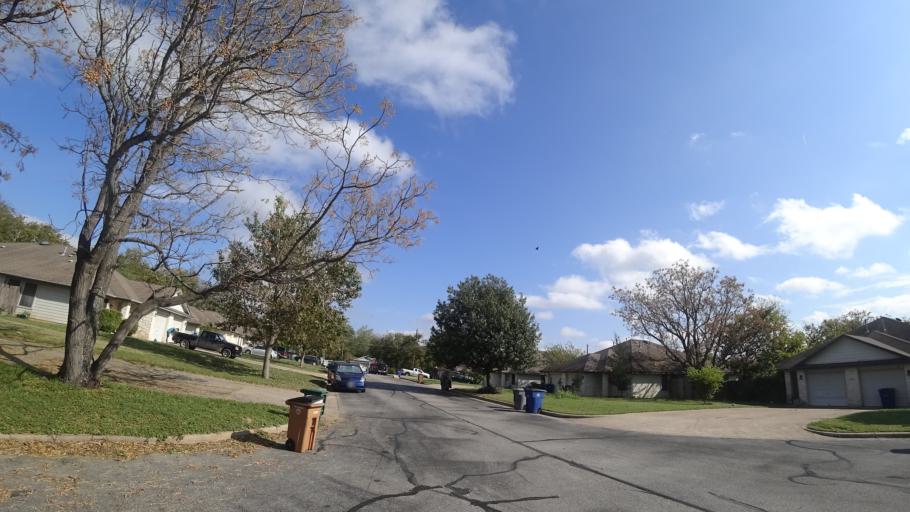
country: US
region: Texas
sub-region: Travis County
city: Shady Hollow
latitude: 30.1921
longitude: -97.8276
